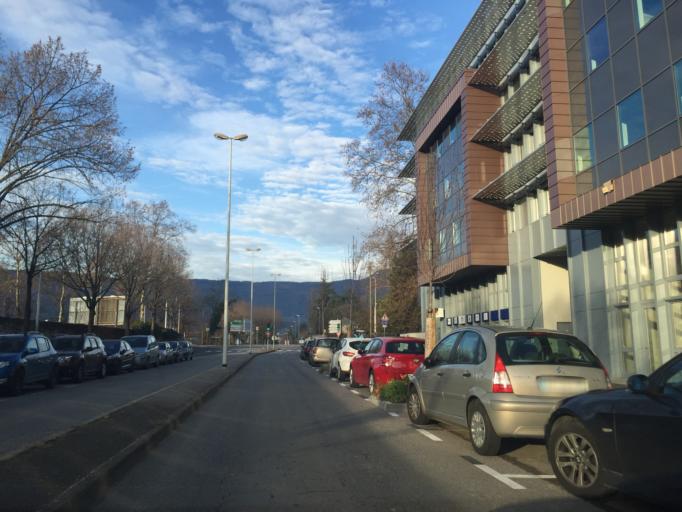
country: FR
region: Rhone-Alpes
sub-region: Departement de la Savoie
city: Cognin
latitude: 45.5757
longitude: 5.9084
